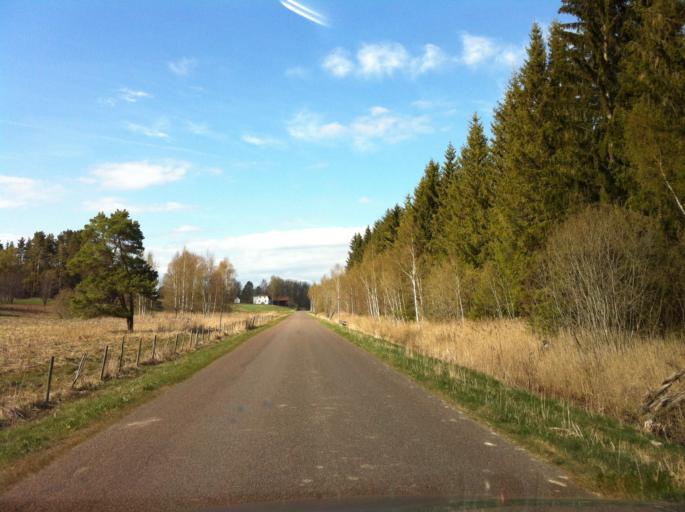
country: SE
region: Kalmar
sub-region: Vimmerby Kommun
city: Sodra Vi
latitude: 57.8451
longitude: 15.8423
